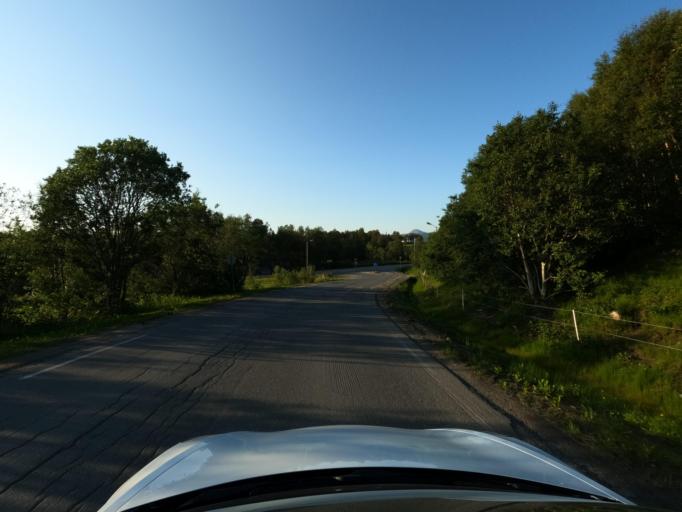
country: NO
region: Troms
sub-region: Skanland
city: Evenskjer
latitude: 68.4909
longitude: 16.7158
